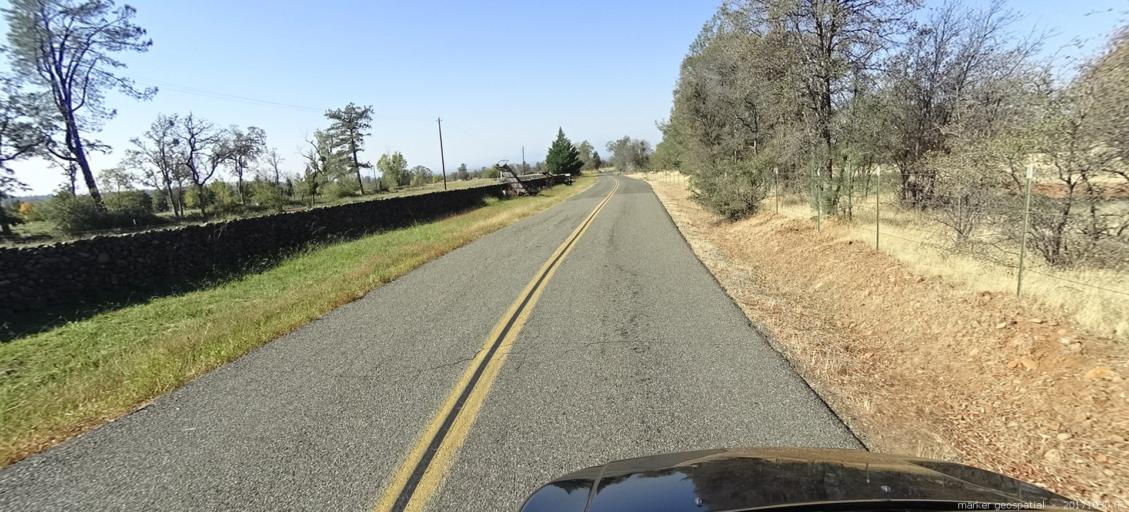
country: US
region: California
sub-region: Shasta County
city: Shingletown
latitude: 40.6379
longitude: -121.9566
